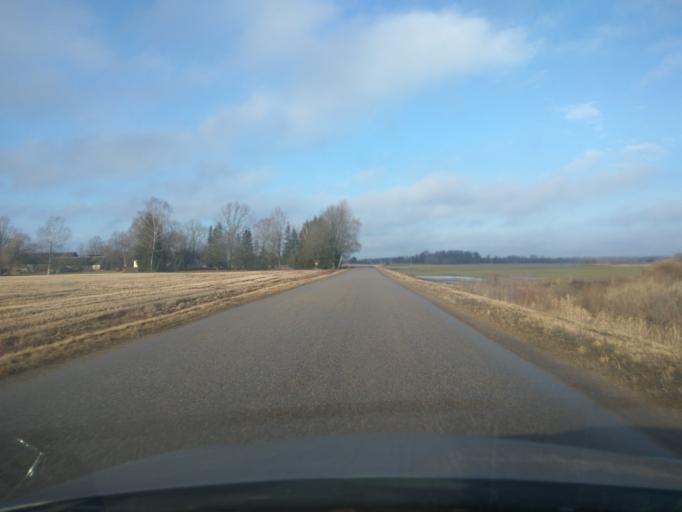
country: LV
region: Saldus Rajons
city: Saldus
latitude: 56.8166
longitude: 22.3792
